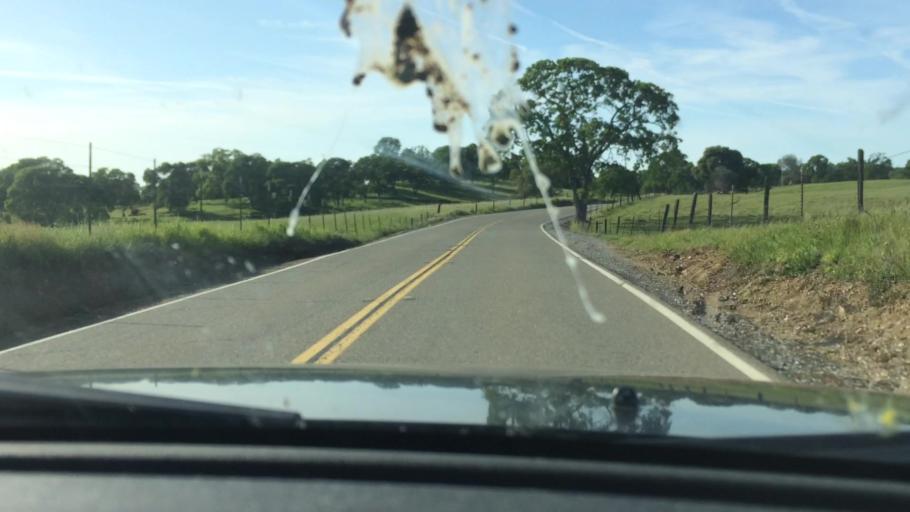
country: US
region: California
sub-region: Amador County
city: Plymouth
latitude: 38.4895
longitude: -120.9340
